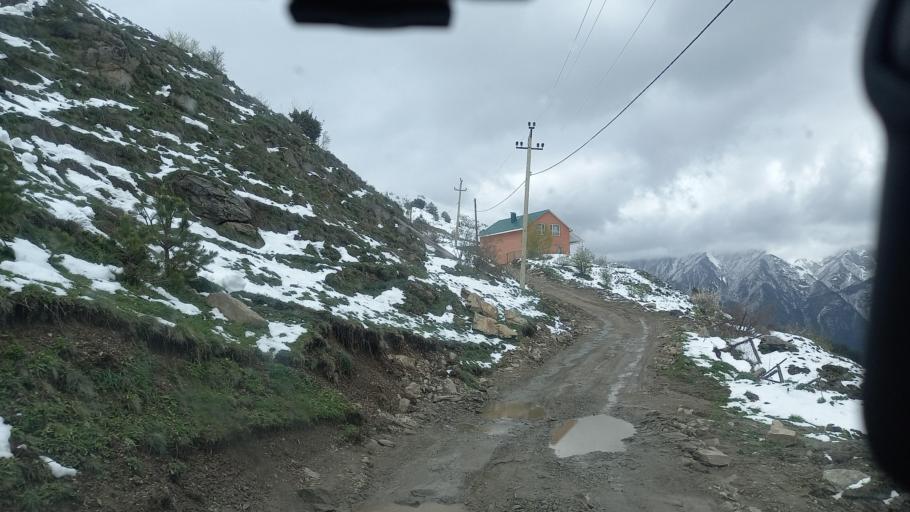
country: RU
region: North Ossetia
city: Mizur
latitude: 42.8056
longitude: 43.9473
